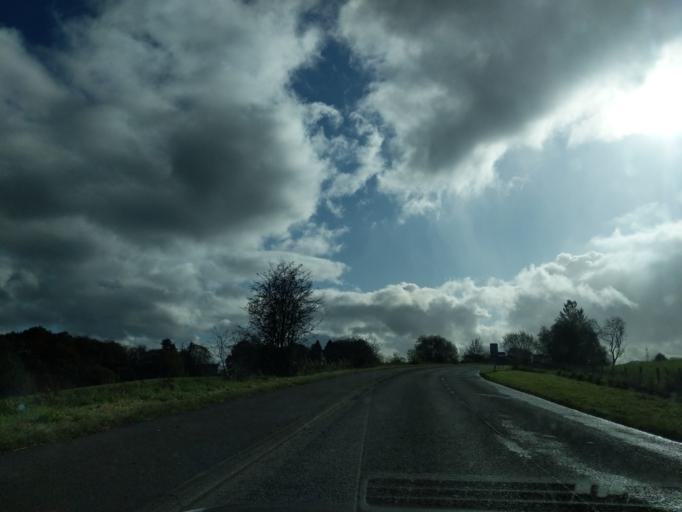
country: GB
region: Scotland
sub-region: Dumfries and Galloway
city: Moffat
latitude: 55.3210
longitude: -3.4453
